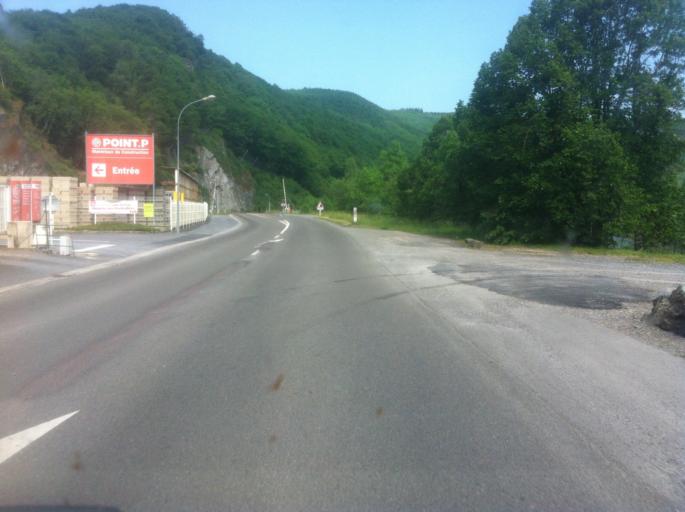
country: FR
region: Champagne-Ardenne
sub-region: Departement des Ardennes
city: Fumay
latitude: 49.9952
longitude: 4.6969
